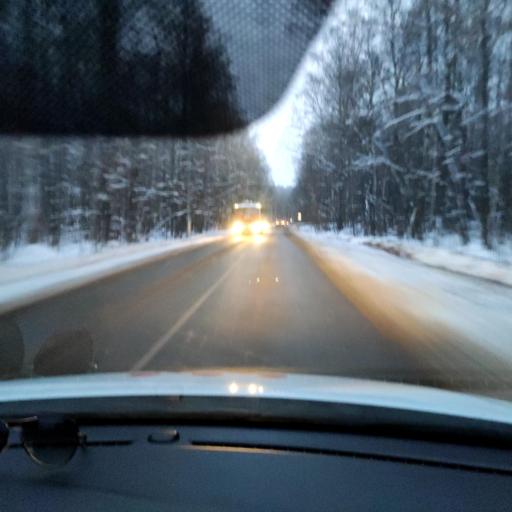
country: RU
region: Tatarstan
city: Vysokaya Gora
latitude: 55.9337
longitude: 49.1697
